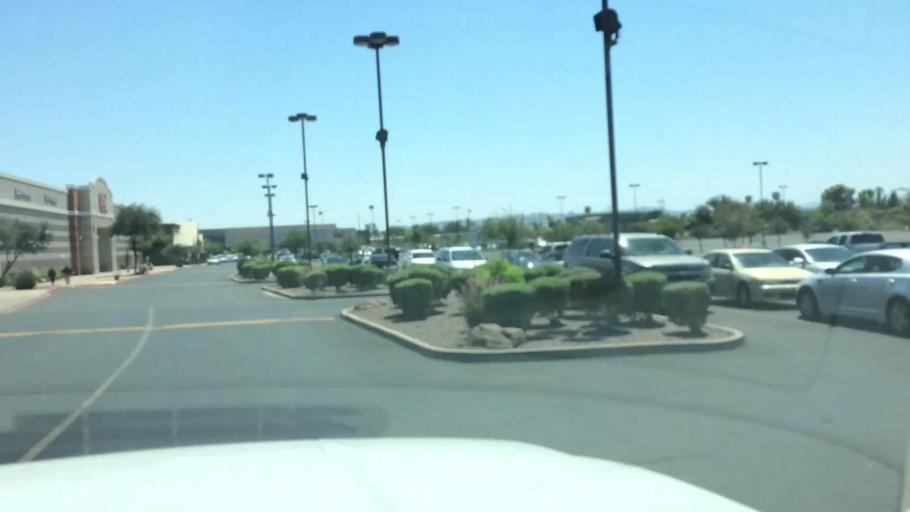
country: US
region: Arizona
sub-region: Maricopa County
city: Paradise Valley
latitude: 33.4765
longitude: -111.9847
